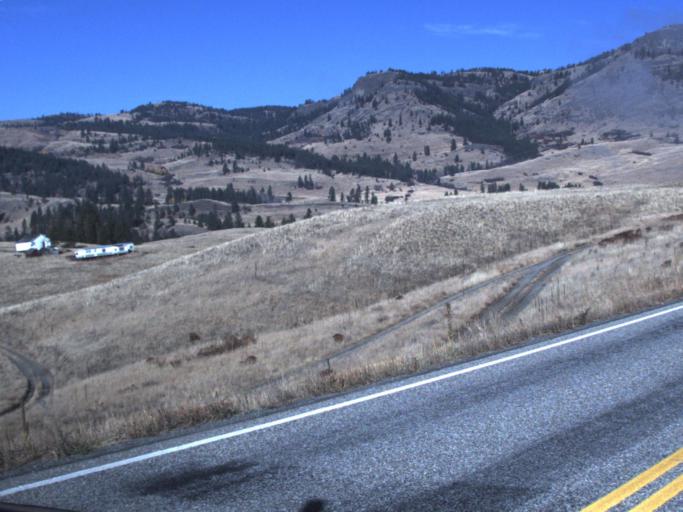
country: US
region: Washington
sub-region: Ferry County
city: Republic
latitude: 48.7607
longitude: -118.6471
